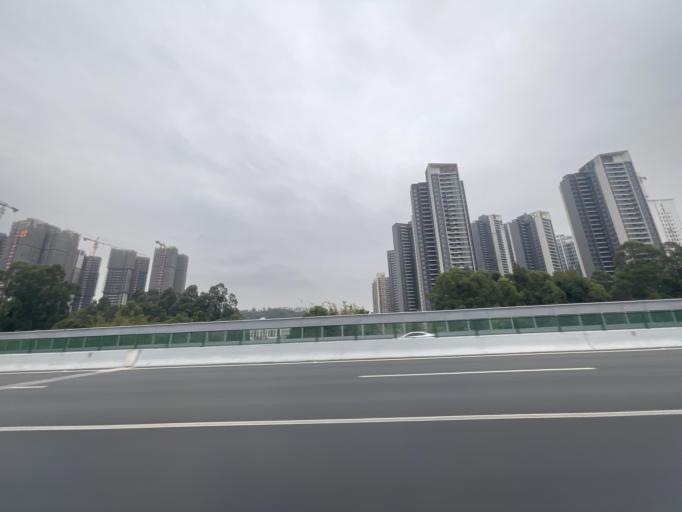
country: CN
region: Guangdong
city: Huangge
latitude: 22.7906
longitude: 113.5109
